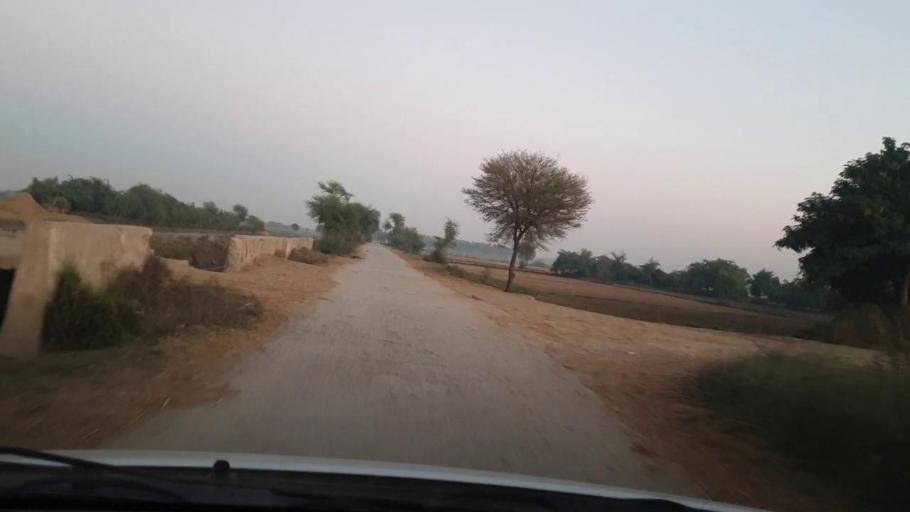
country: PK
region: Sindh
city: Khairpur Nathan Shah
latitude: 27.1421
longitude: 67.7151
